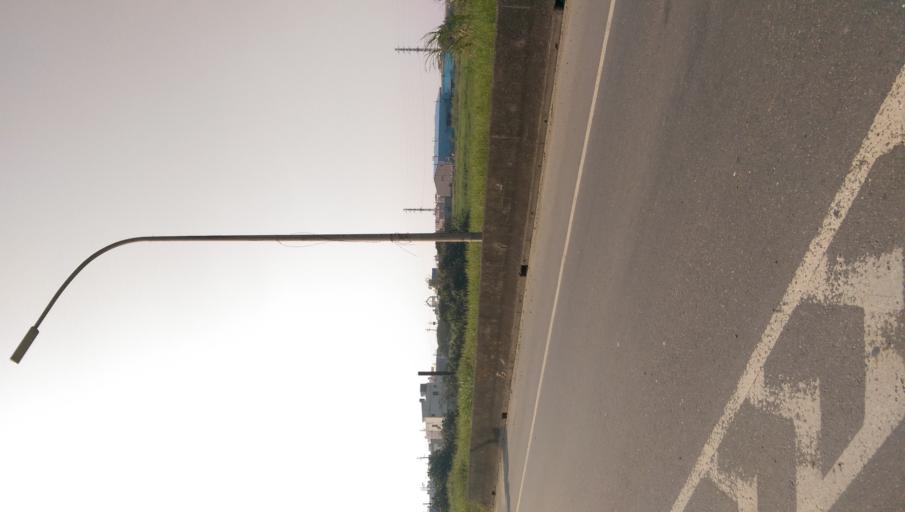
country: TW
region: Taiwan
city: Taoyuan City
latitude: 25.1074
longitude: 121.2467
